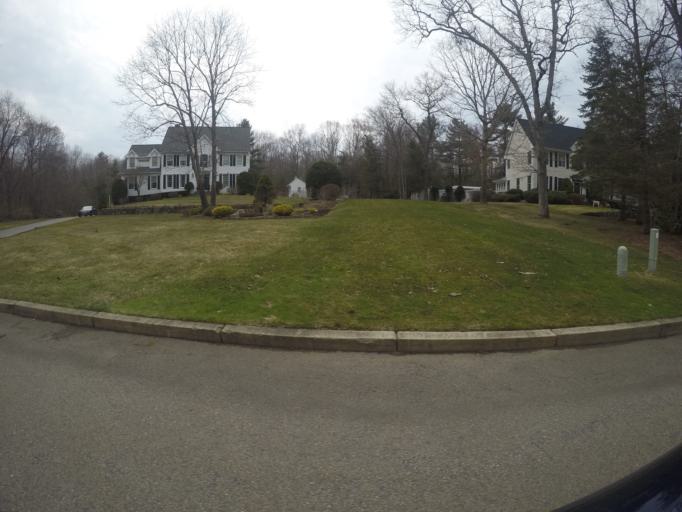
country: US
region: Massachusetts
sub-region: Norfolk County
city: Stoughton
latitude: 42.0853
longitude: -71.1049
